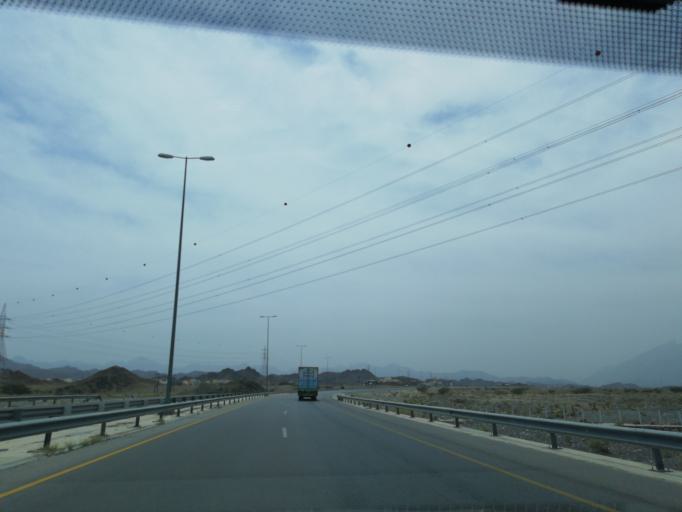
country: OM
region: Muhafazat ad Dakhiliyah
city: Sufalat Sama'il
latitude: 23.2675
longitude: 57.9368
